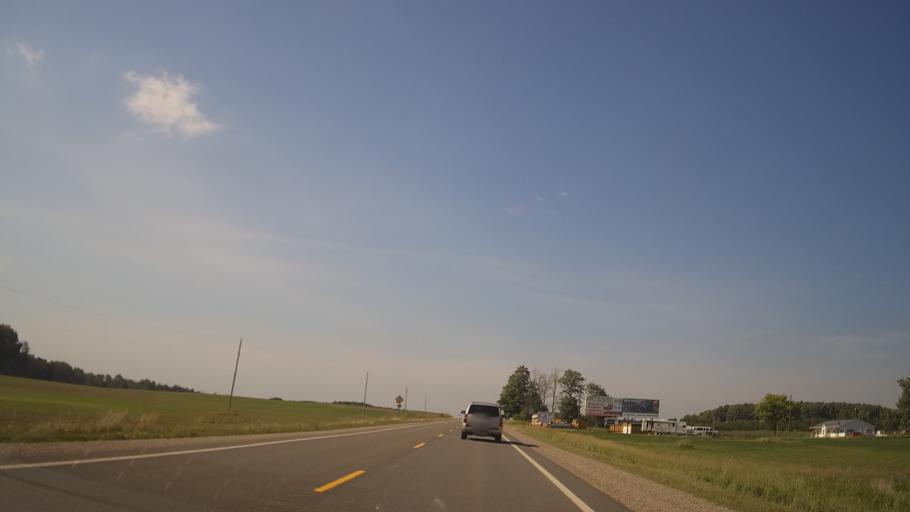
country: US
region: Michigan
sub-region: Ogemaw County
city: West Branch
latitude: 44.2668
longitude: -84.1257
